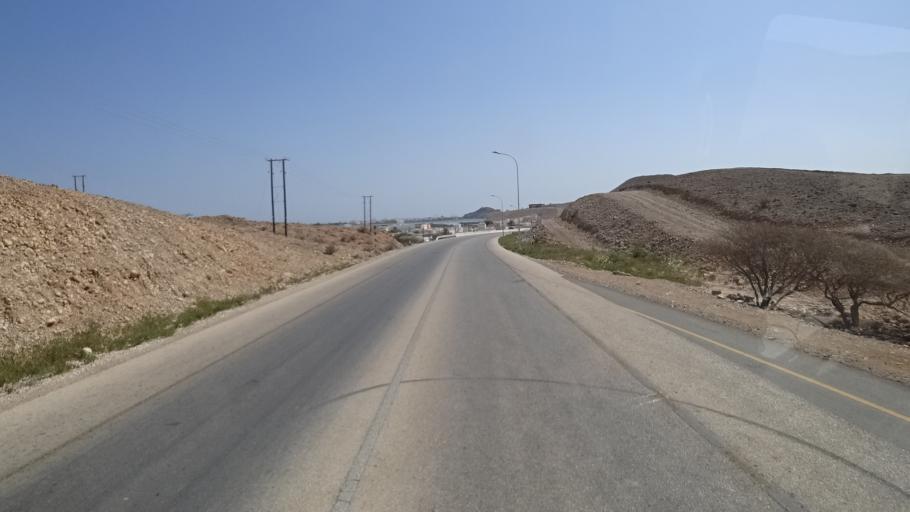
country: OM
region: Ash Sharqiyah
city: Sur
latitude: 22.5465
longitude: 59.5212
